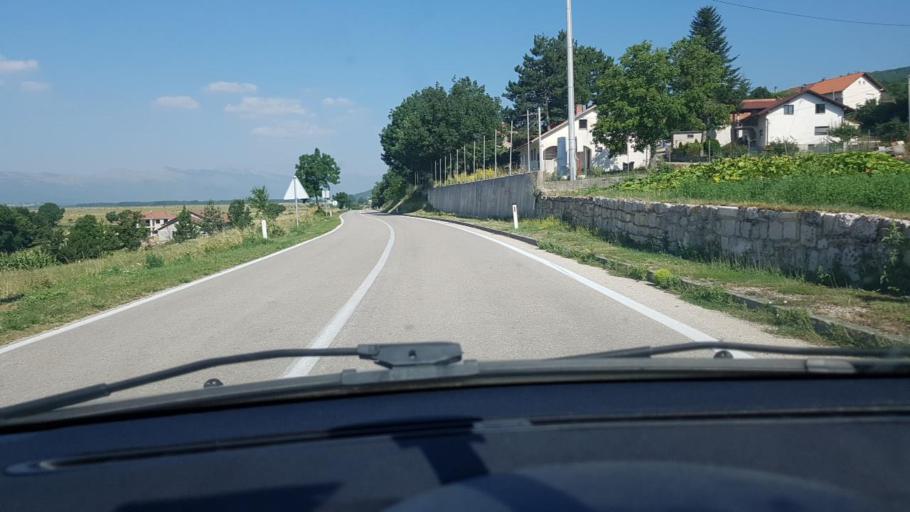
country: BA
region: Federation of Bosnia and Herzegovina
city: Orguz
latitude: 43.8730
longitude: 16.8711
